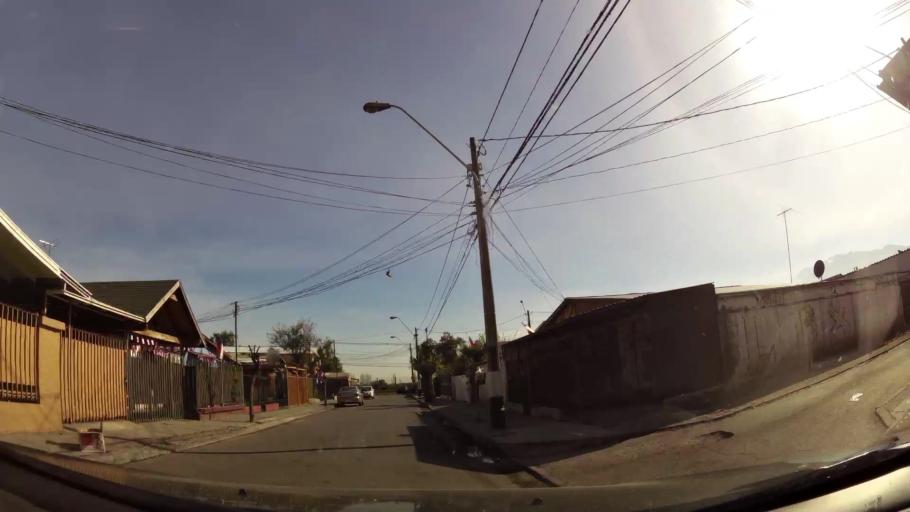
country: CL
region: Santiago Metropolitan
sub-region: Provincia de Cordillera
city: Puente Alto
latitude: -33.6065
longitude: -70.5993
